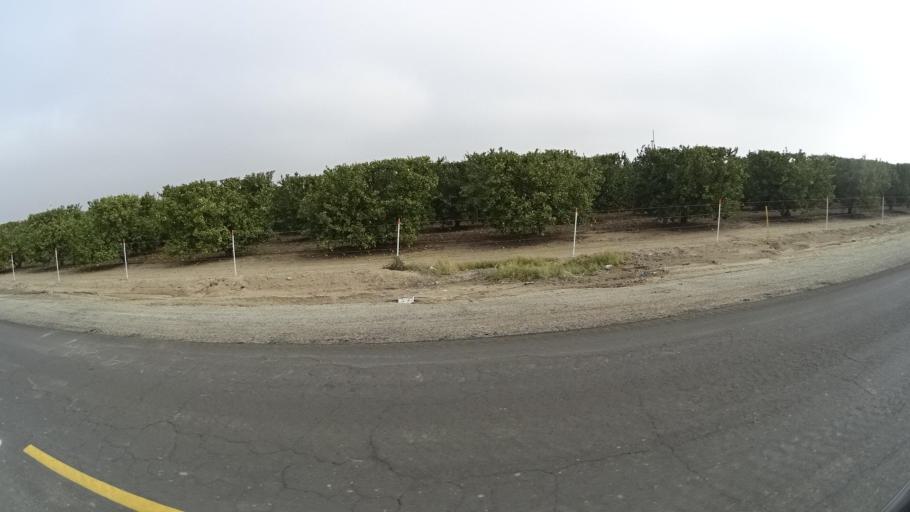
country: US
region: California
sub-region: Kern County
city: Maricopa
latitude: 35.0649
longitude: -119.3138
